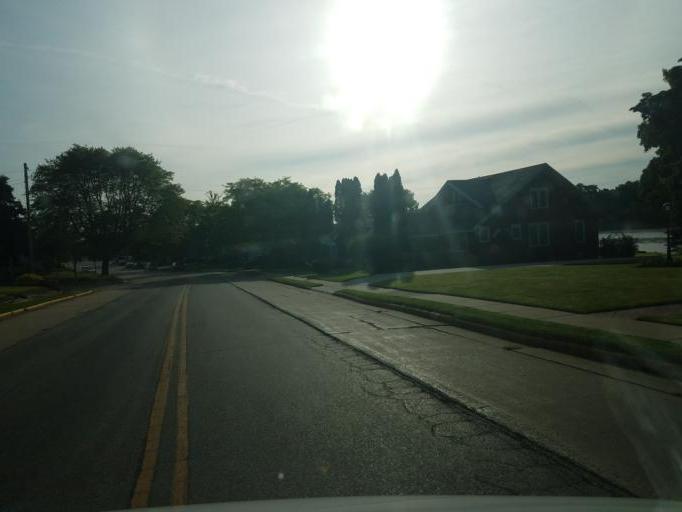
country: US
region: Wisconsin
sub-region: Vernon County
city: Hillsboro
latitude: 43.6488
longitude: -90.3426
